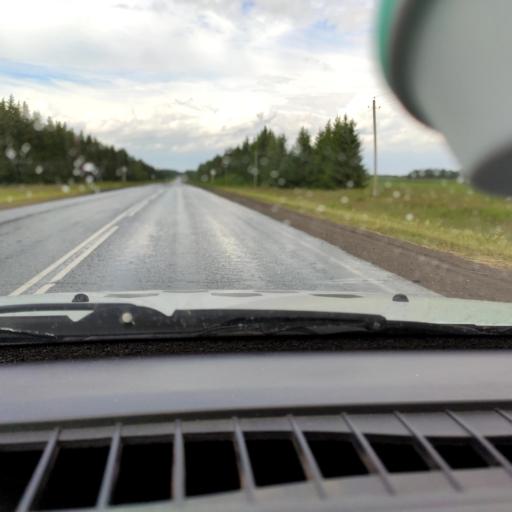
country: RU
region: Perm
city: Orda
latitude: 57.2083
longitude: 56.9305
